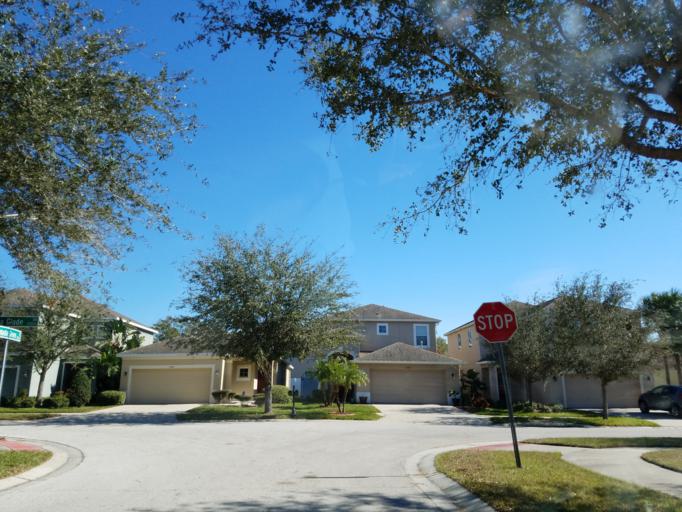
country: US
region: Florida
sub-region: Hillsborough County
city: Riverview
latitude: 27.8071
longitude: -82.3361
